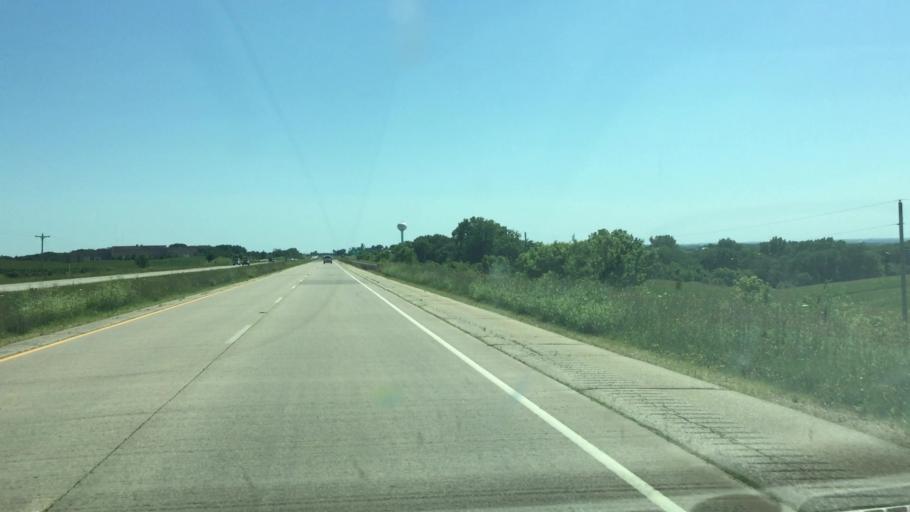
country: US
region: Wisconsin
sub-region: Grant County
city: Dickeyville
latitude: 42.5968
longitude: -90.5981
